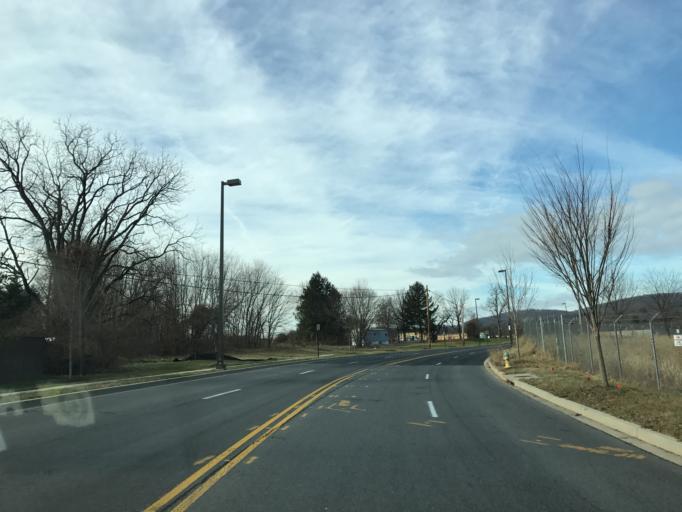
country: US
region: Maryland
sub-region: Frederick County
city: Clover Hill
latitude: 39.4295
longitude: -77.4525
